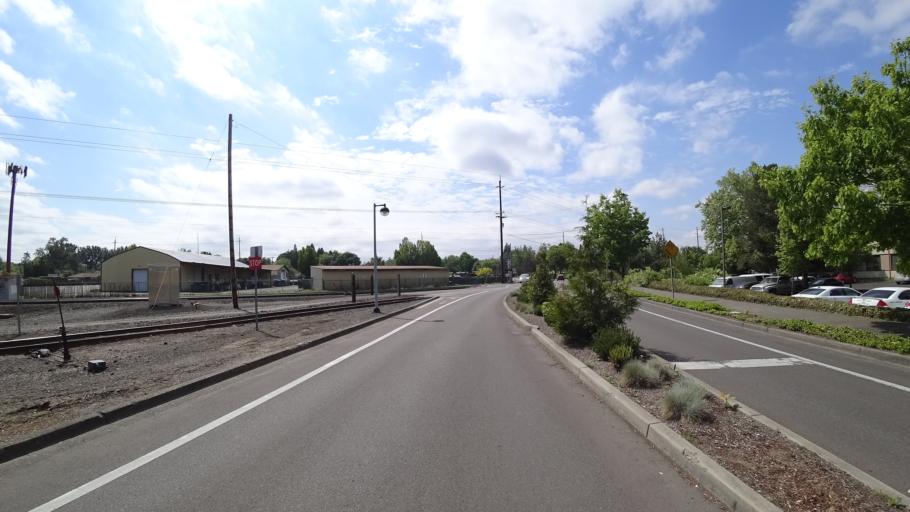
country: US
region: Oregon
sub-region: Washington County
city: Beaverton
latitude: 45.4822
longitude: -122.7949
